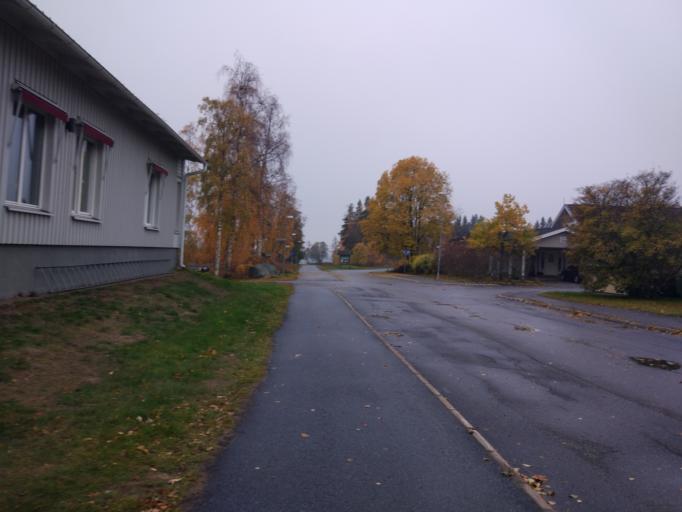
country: SE
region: Vaesterbotten
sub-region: Umea Kommun
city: Holmsund
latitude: 63.6980
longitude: 20.3678
